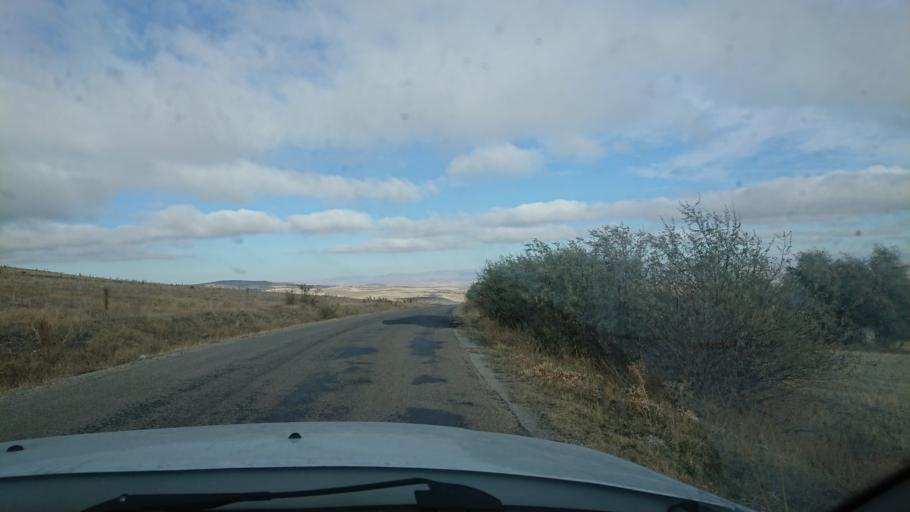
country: TR
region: Aksaray
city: Ortakoy
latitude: 38.7916
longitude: 33.9967
